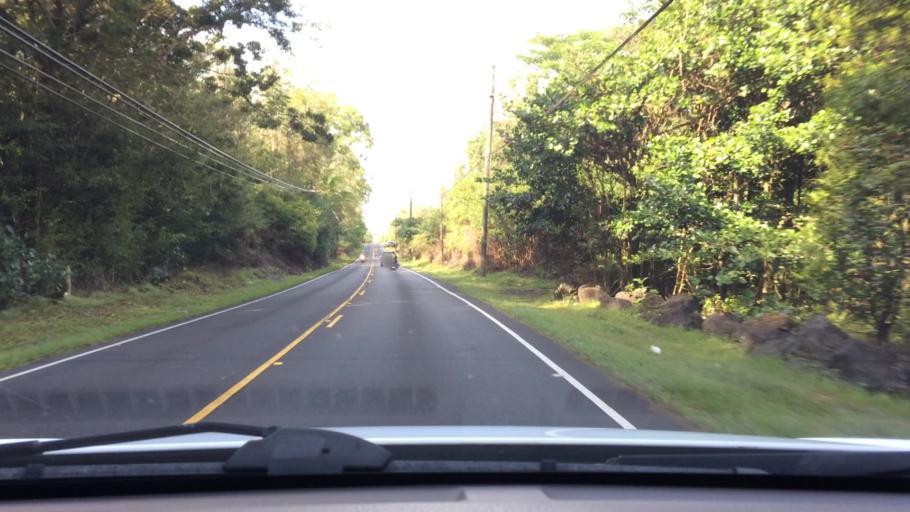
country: US
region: Hawaii
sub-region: Hawaii County
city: Hawaiian Paradise Park
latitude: 19.5056
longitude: -154.9507
